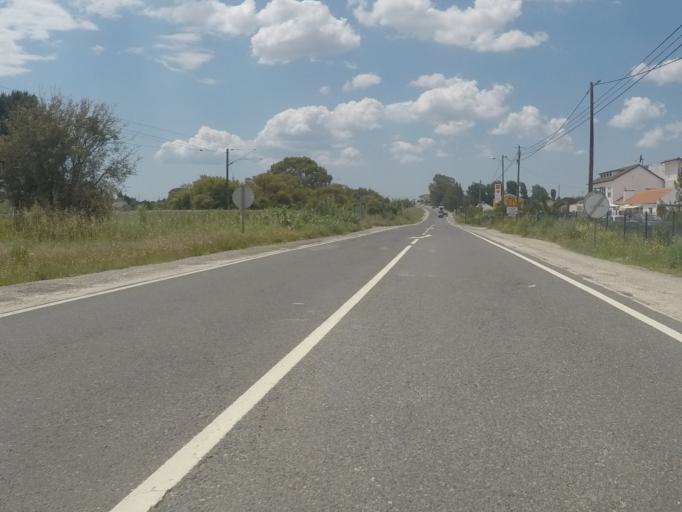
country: PT
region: Setubal
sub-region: Setubal
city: Setubal
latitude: 38.5685
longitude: -8.7644
